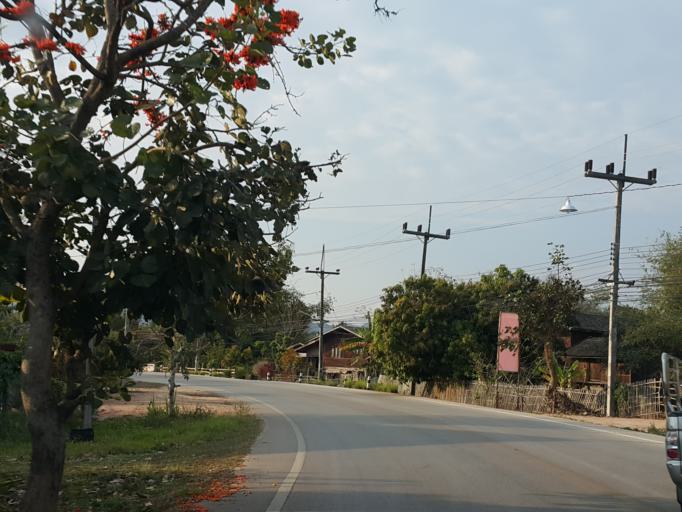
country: TH
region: Lampang
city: Chae Hom
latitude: 18.5434
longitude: 99.4804
